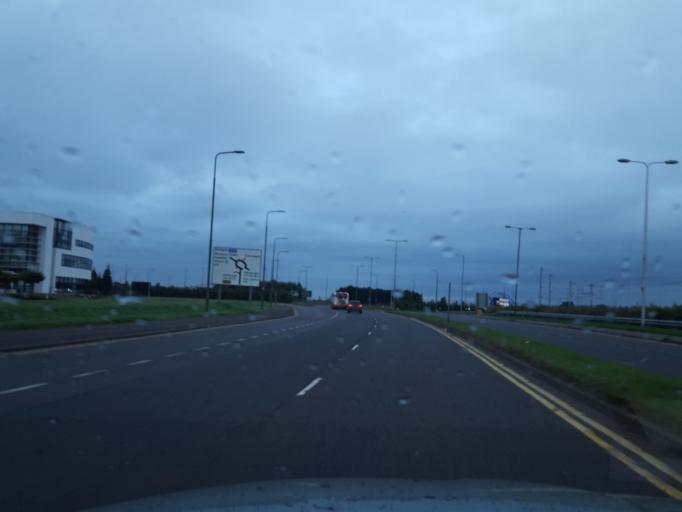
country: GB
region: Scotland
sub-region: Edinburgh
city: Currie
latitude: 55.9377
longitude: -3.3183
